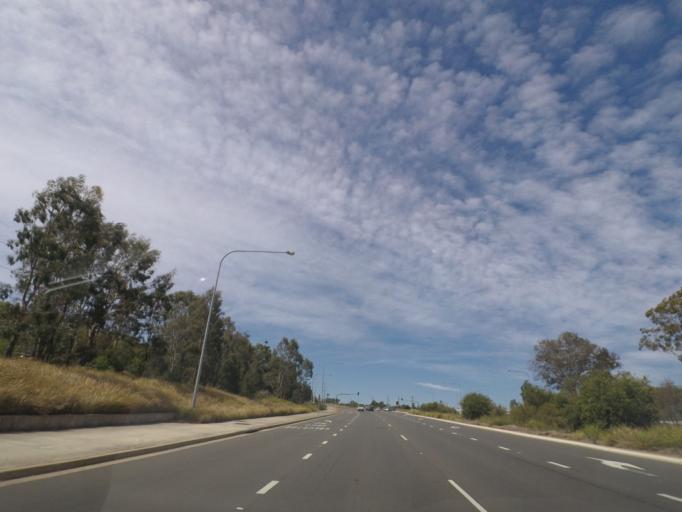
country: AU
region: New South Wales
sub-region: Camden
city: Narellan
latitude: -34.0308
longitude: 150.7513
